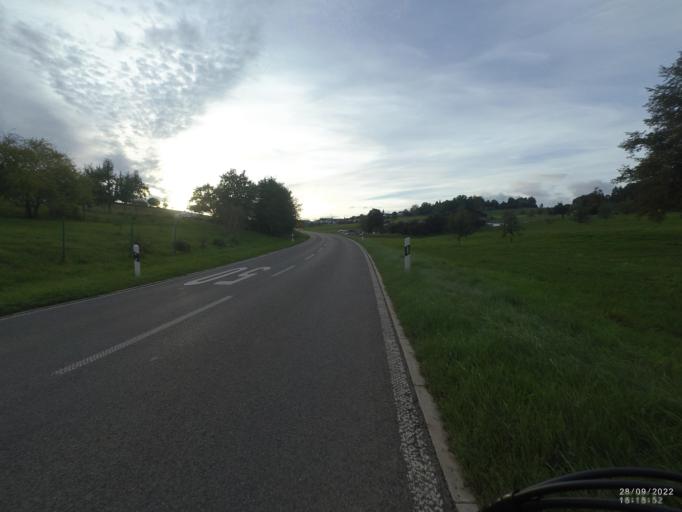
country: DE
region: Baden-Wuerttemberg
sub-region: Regierungsbezirk Stuttgart
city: Bortlingen
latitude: 48.7494
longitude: 9.6449
